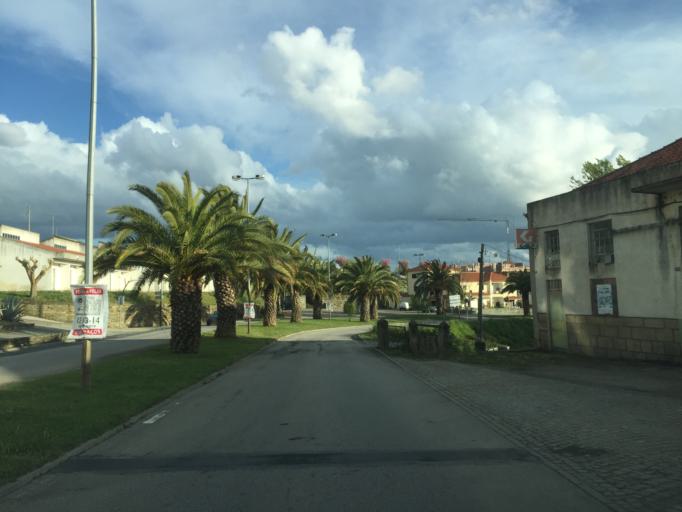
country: PT
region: Braganca
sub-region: Alfandega da Fe
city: Alfandega da Fe
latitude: 41.3384
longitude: -6.9625
